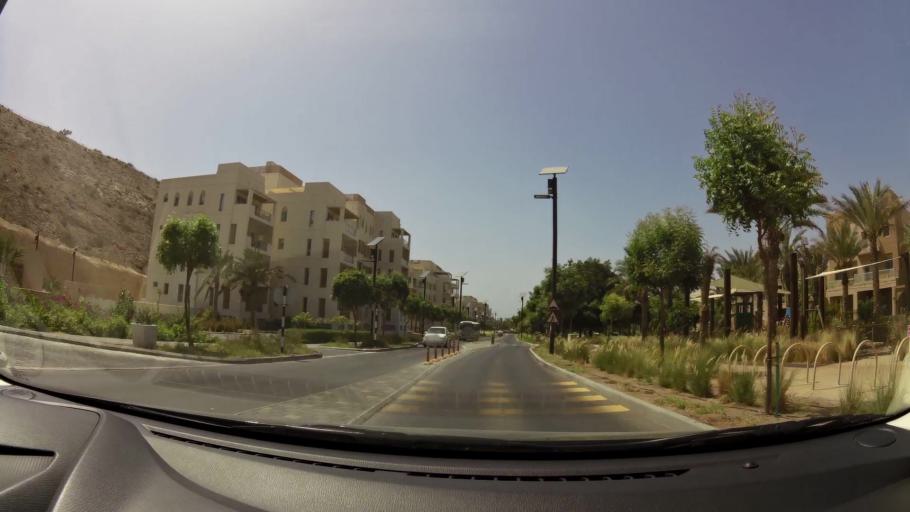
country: OM
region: Muhafazat Masqat
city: Muscat
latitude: 23.6322
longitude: 58.5013
